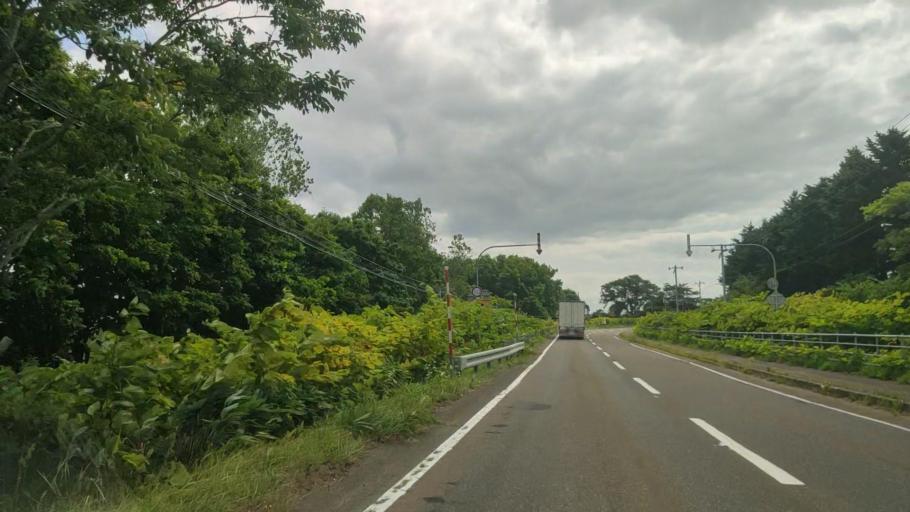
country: JP
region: Hokkaido
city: Rumoi
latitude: 44.5607
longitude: 141.7858
